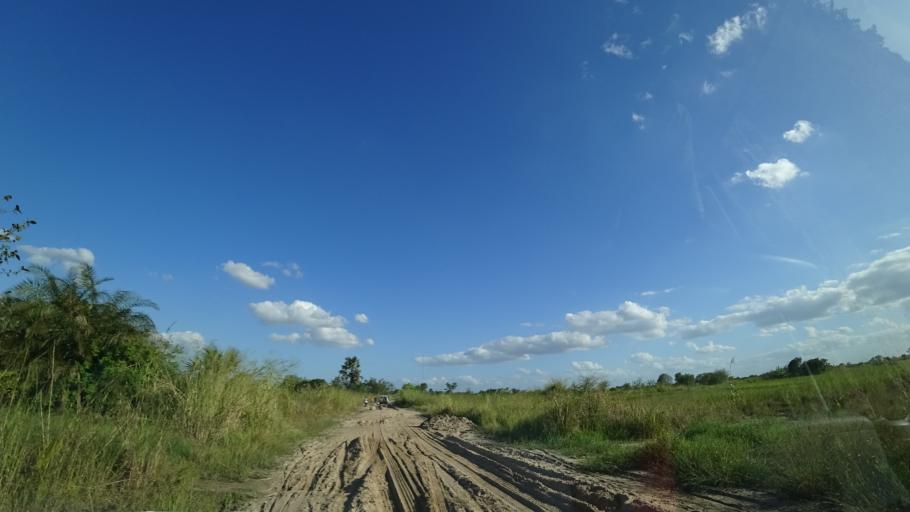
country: MZ
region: Sofala
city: Dondo
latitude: -19.3729
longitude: 34.5924
